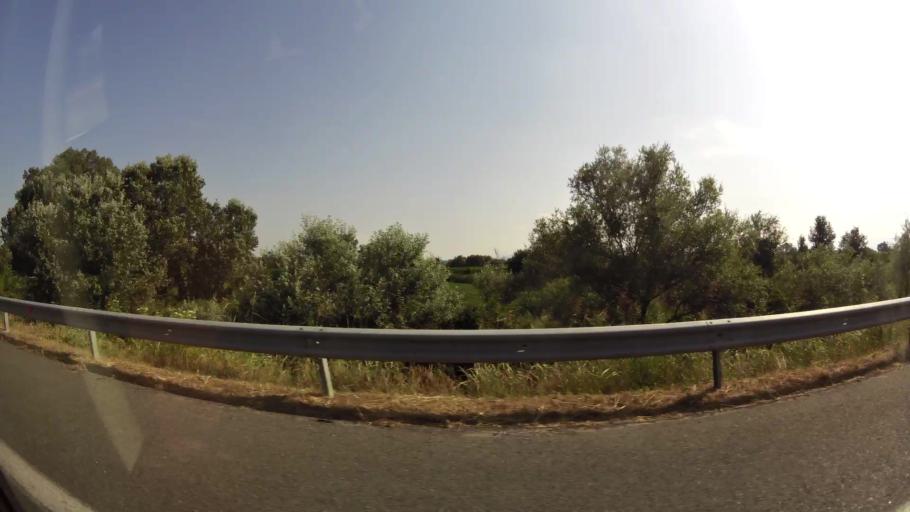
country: GR
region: Central Macedonia
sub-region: Nomos Imathias
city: Agkathia
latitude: 40.5844
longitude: 22.4814
